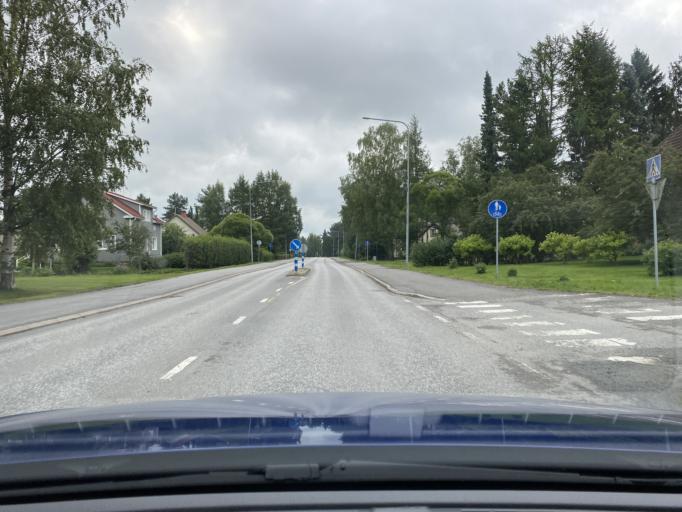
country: FI
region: Ostrobothnia
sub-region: Kyroenmaa
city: Laihia
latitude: 62.9736
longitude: 22.0185
